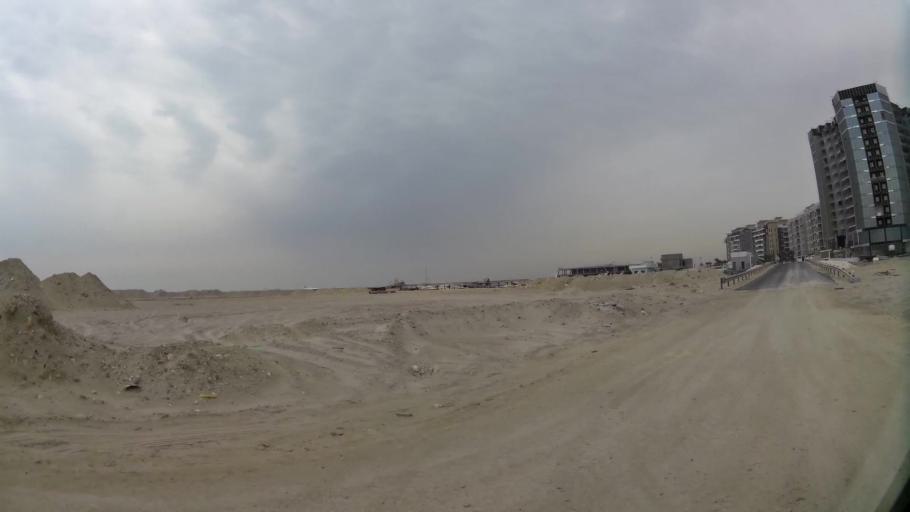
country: BH
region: Central Governorate
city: Dar Kulayb
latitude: 25.8676
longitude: 50.6117
